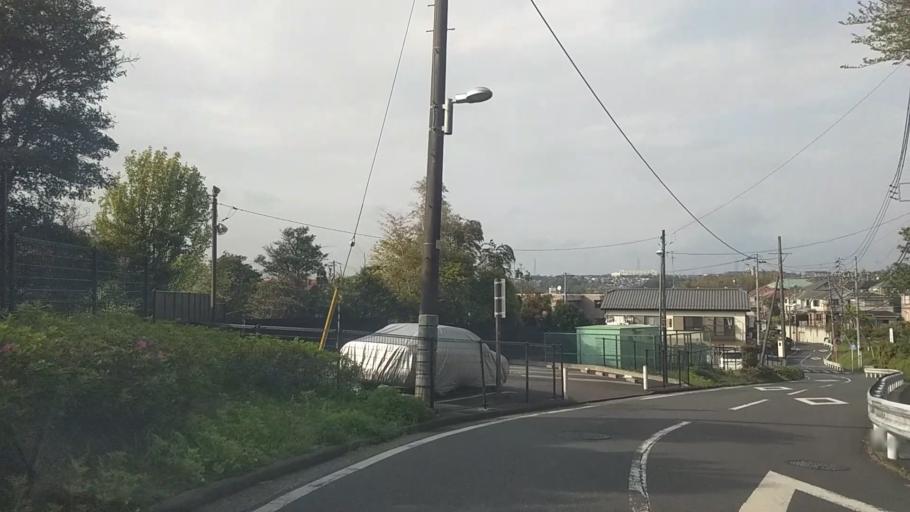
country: JP
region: Kanagawa
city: Kamakura
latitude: 35.3600
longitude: 139.5565
